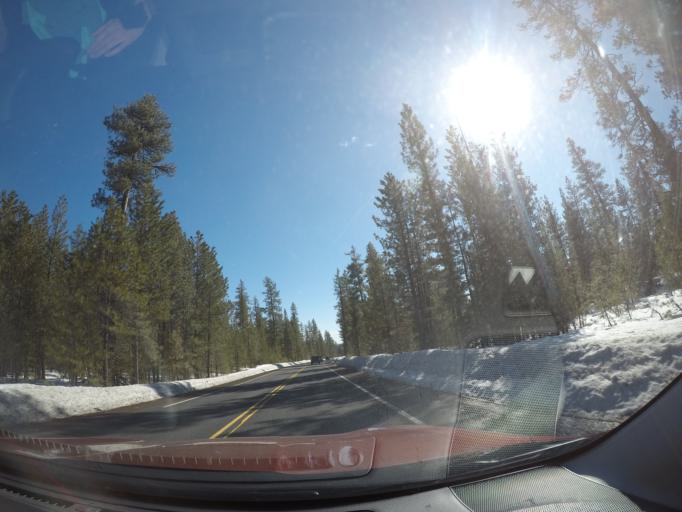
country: US
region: Oregon
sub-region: Deschutes County
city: Three Rivers
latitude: 43.8977
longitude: -121.5918
